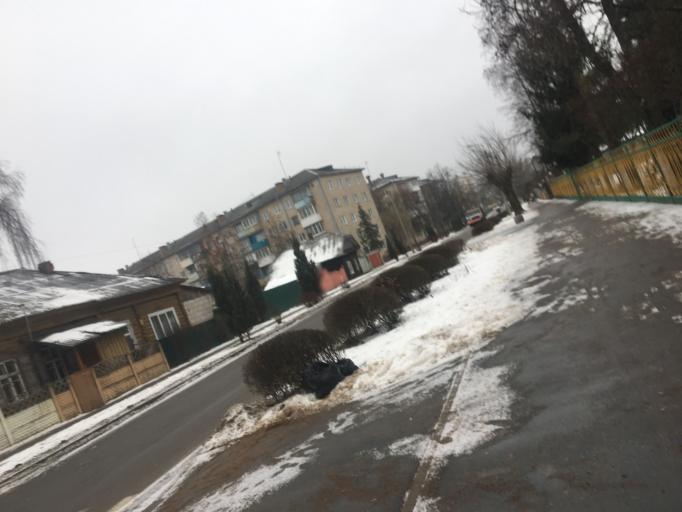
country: BY
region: Mogilev
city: Babruysk
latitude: 53.1524
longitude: 29.2403
